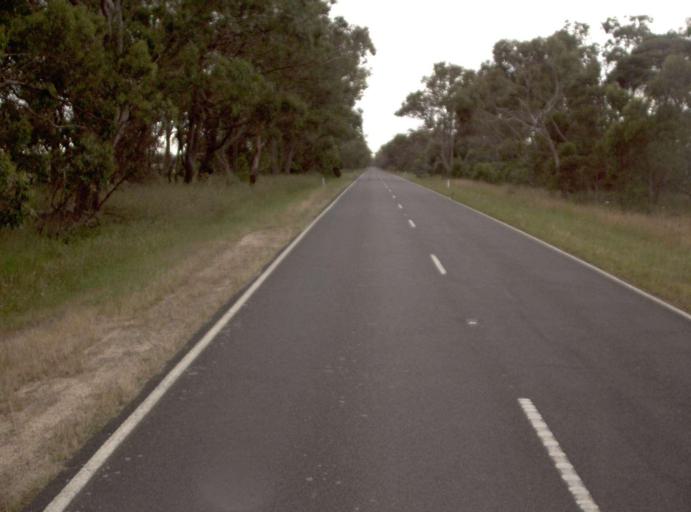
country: AU
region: Victoria
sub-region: Latrobe
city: Traralgon
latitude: -38.5540
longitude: 146.8163
